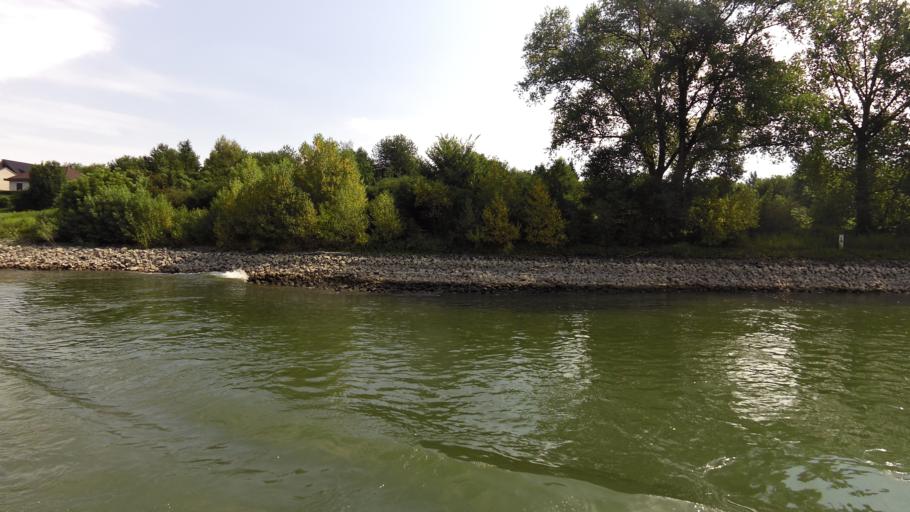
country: DE
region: Rheinland-Pfalz
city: Rheinbreitbach
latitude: 50.6160
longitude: 7.2146
